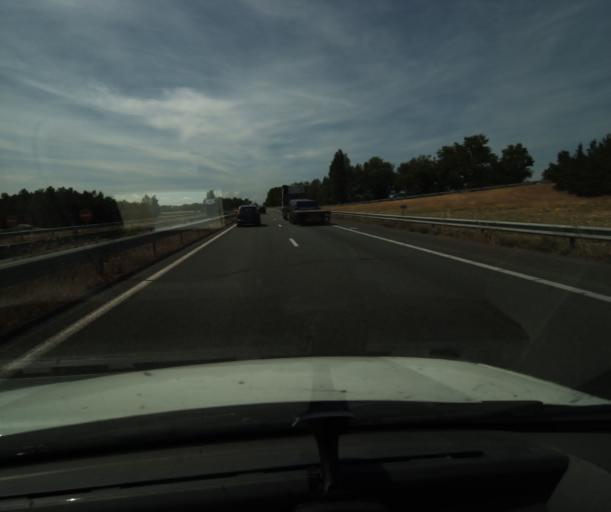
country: FR
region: Languedoc-Roussillon
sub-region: Departement de l'Aude
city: Bram
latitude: 43.2366
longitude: 2.0970
